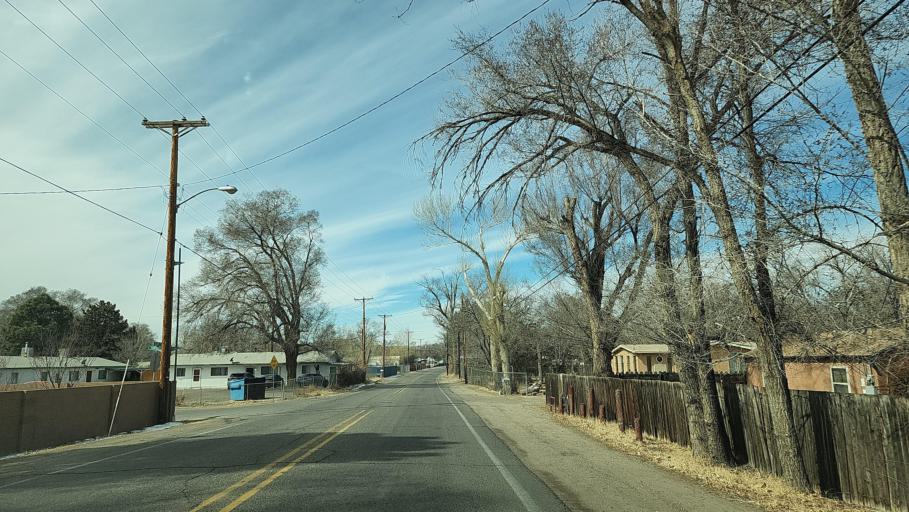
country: US
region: New Mexico
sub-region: Bernalillo County
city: South Valley
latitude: 35.0363
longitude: -106.6923
